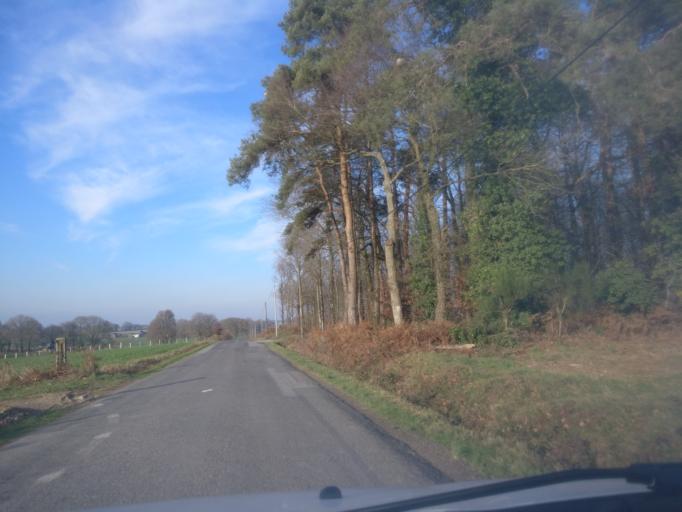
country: FR
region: Brittany
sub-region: Departement d'Ille-et-Vilaine
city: Livre-sur-Changeon
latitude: 48.1971
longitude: -1.3087
